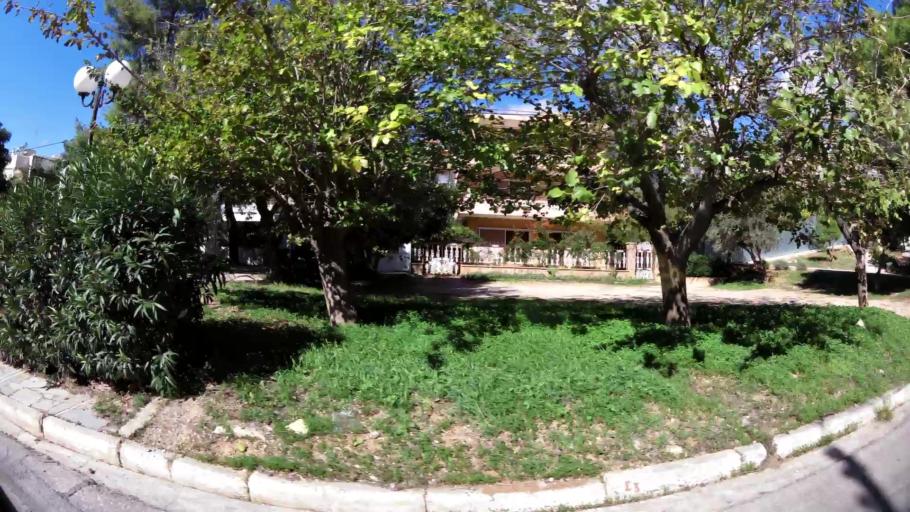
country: GR
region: Attica
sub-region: Nomarchia Anatolikis Attikis
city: Voula
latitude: 37.8426
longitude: 23.7774
